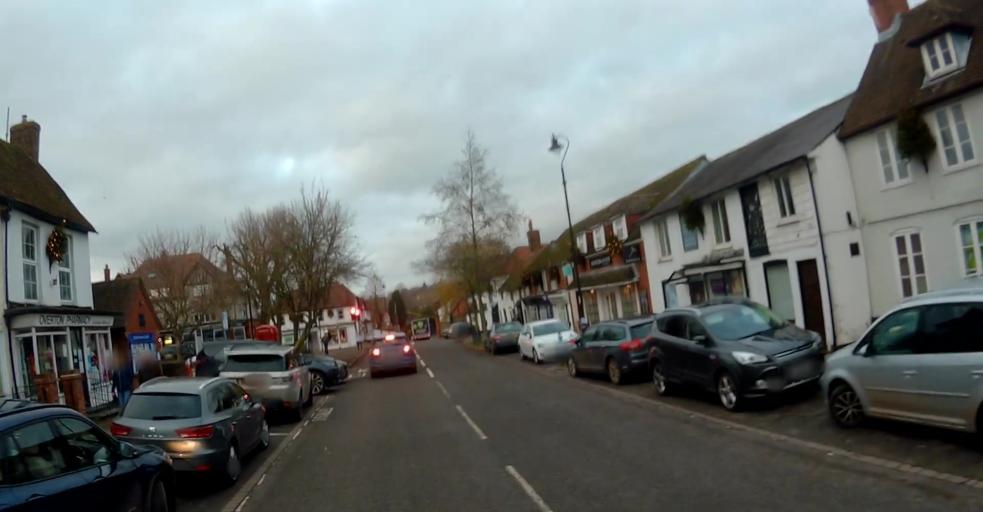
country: GB
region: England
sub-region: Hampshire
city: Overton
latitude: 51.2433
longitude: -1.2630
